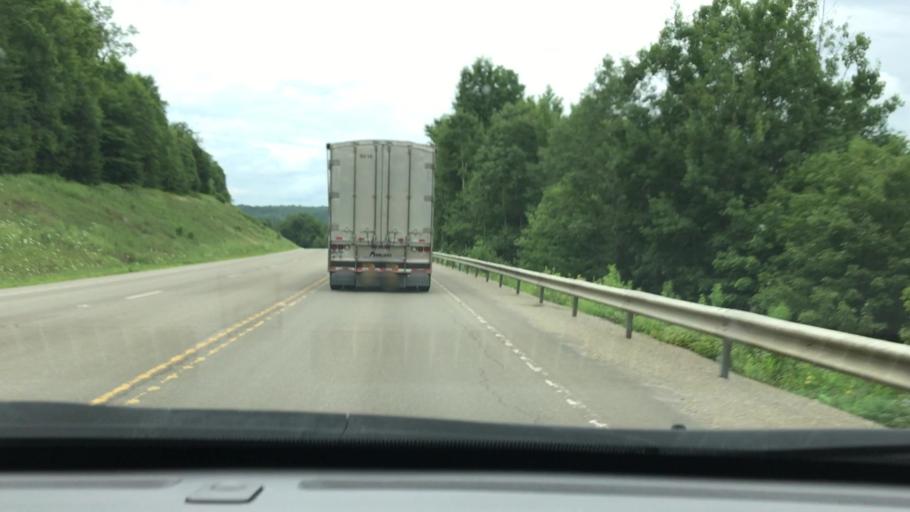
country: US
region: Pennsylvania
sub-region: McKean County
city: Kane
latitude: 41.7454
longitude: -78.6861
